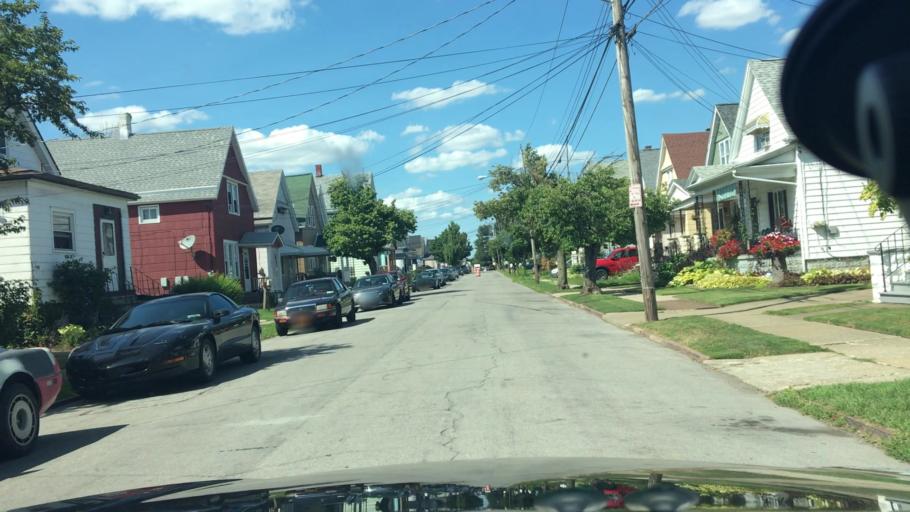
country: US
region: New York
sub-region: Erie County
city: West Seneca
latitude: 42.8691
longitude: -78.8059
